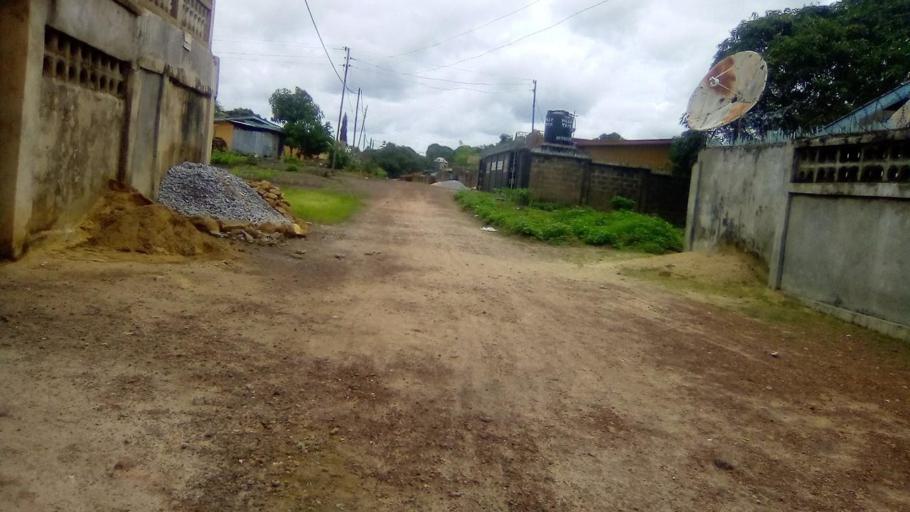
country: SL
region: Southern Province
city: Bo
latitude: 7.9427
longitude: -11.7389
